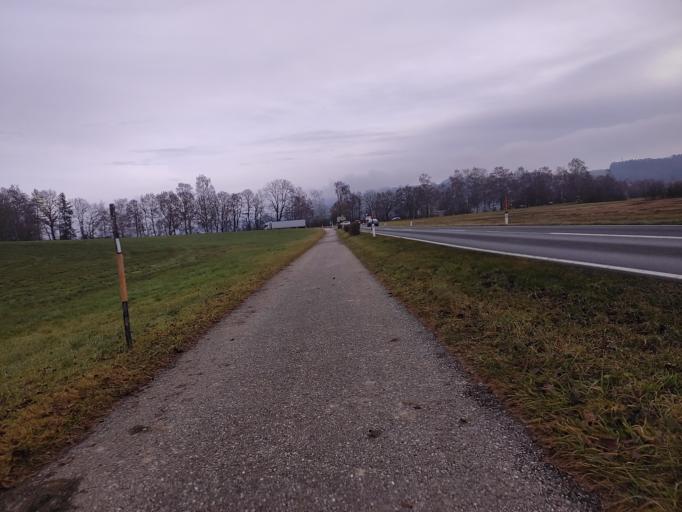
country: AT
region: Salzburg
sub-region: Politischer Bezirk Salzburg-Umgebung
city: Mattsee
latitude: 47.9835
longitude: 13.1010
